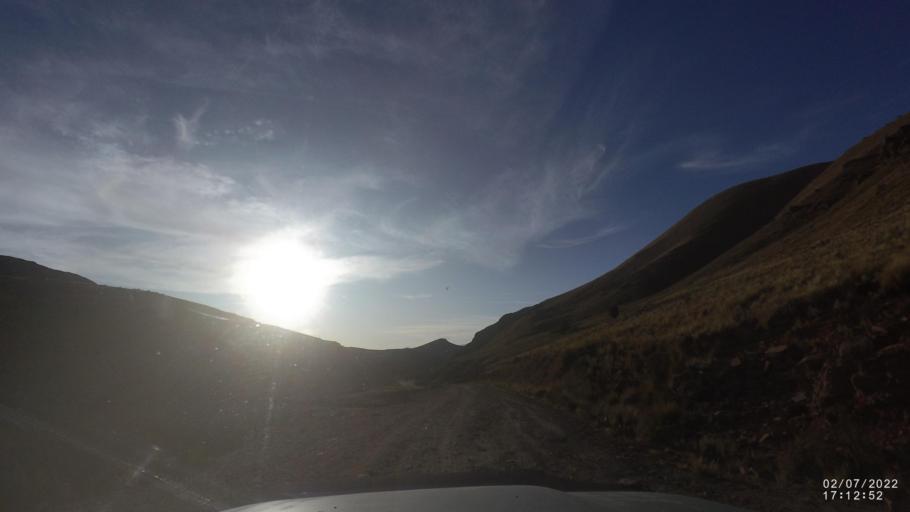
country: BO
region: Cochabamba
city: Irpa Irpa
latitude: -17.8824
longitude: -66.5731
